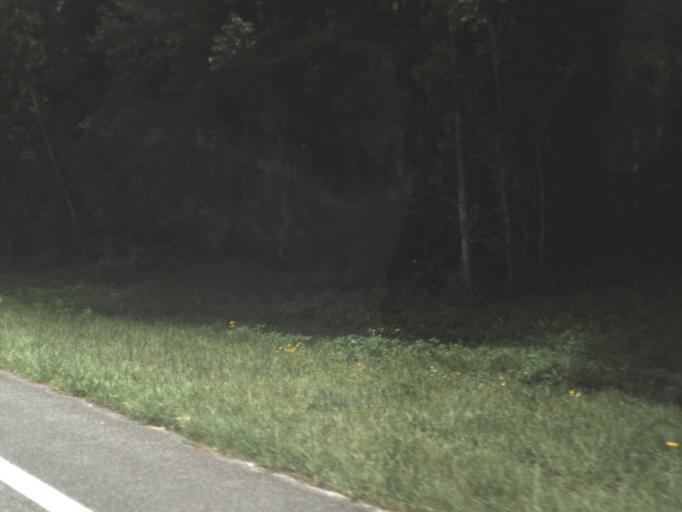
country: US
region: Florida
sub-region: Alachua County
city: High Springs
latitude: 29.8757
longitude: -82.6581
